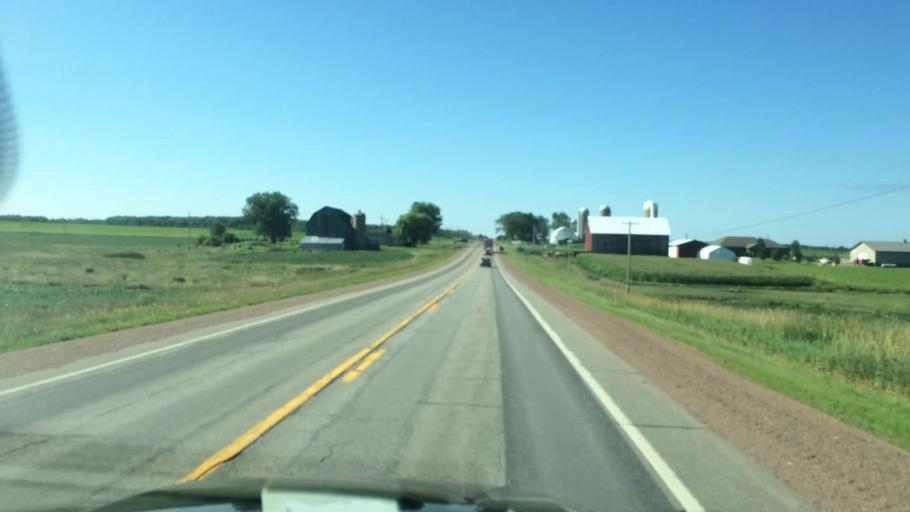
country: US
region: Wisconsin
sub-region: Marathon County
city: Stratford
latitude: 44.9054
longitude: -90.0787
